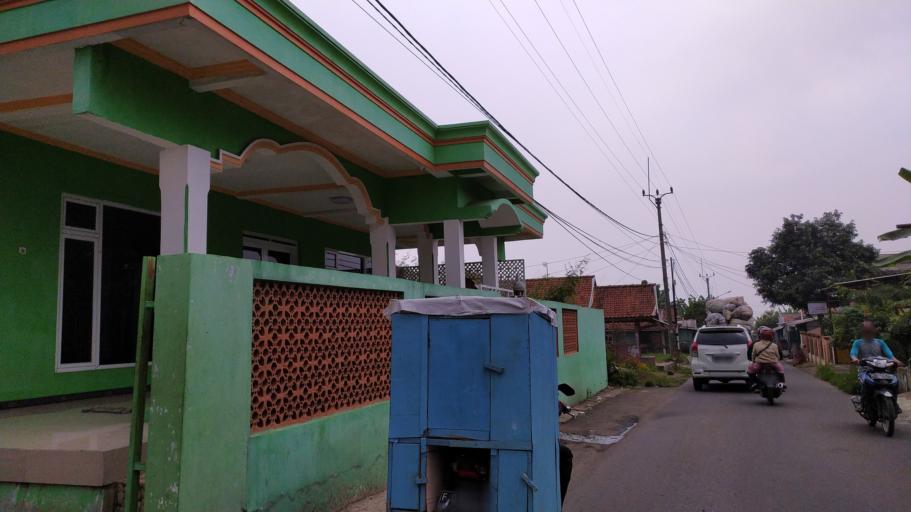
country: ID
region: West Java
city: Ciampea
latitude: -6.5980
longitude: 106.7040
